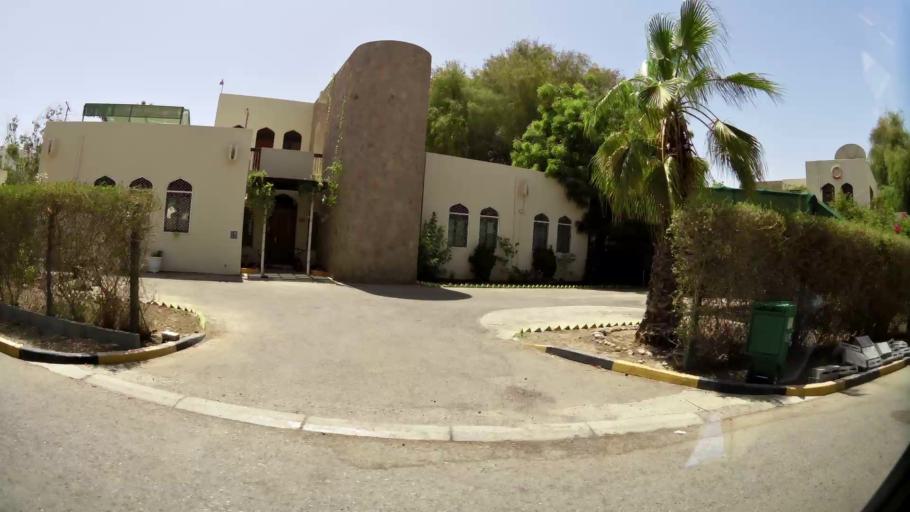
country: OM
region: Muhafazat Masqat
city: Bawshar
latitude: 23.5911
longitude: 58.3986
